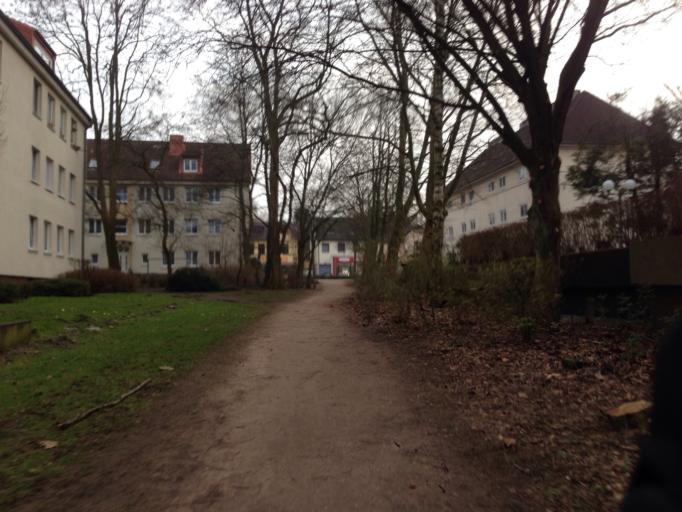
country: DE
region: Hamburg
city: Wandsbek
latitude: 53.5804
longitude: 10.0996
